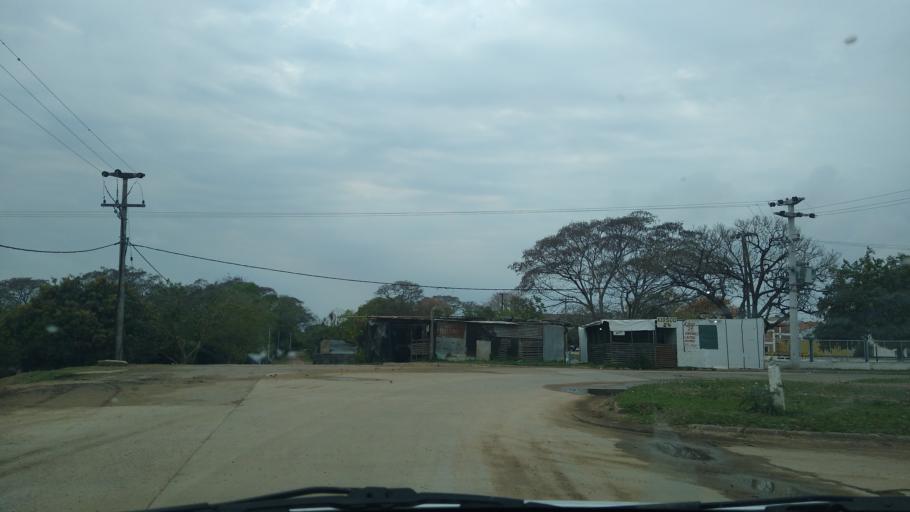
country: AR
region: Chaco
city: Barranqueras
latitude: -27.4699
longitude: -58.9078
